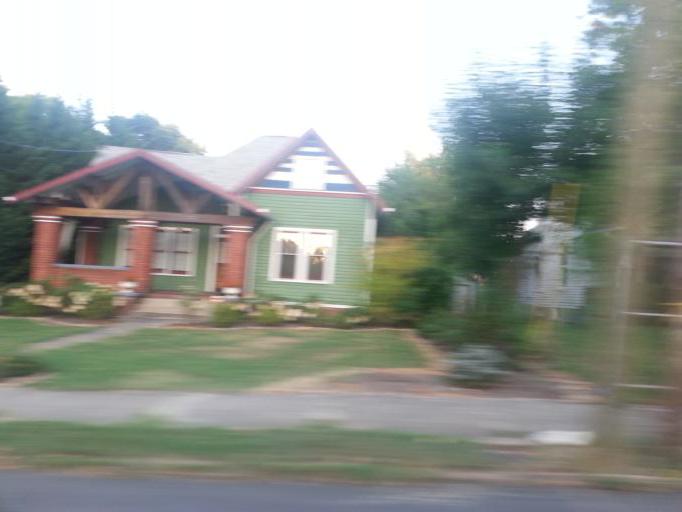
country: US
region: Tennessee
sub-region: Knox County
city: Knoxville
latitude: 35.9854
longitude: -83.9233
